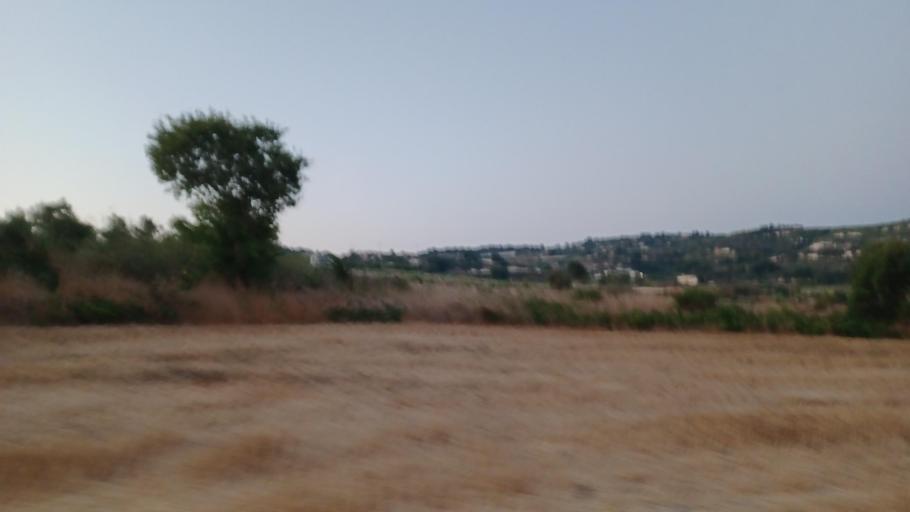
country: CY
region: Pafos
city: Mesogi
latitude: 34.8690
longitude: 32.4970
